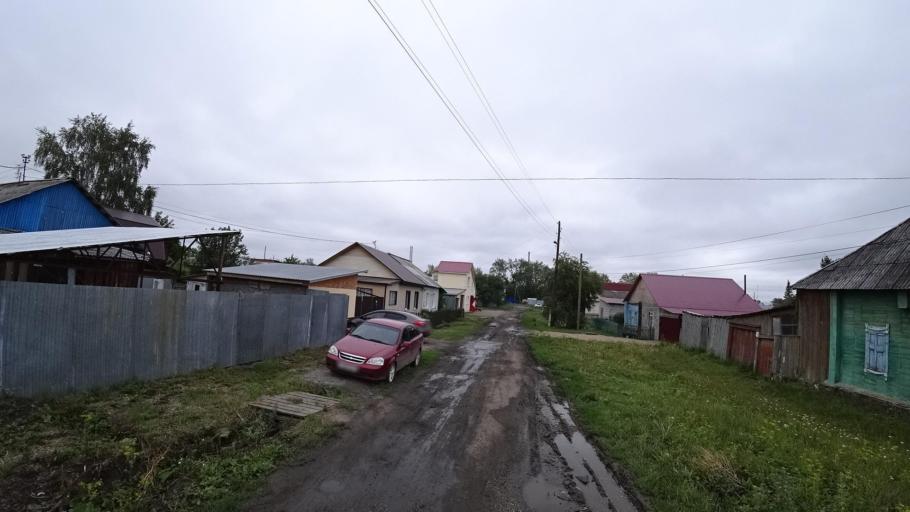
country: RU
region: Sverdlovsk
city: Kamyshlov
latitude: 56.8477
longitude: 62.7651
